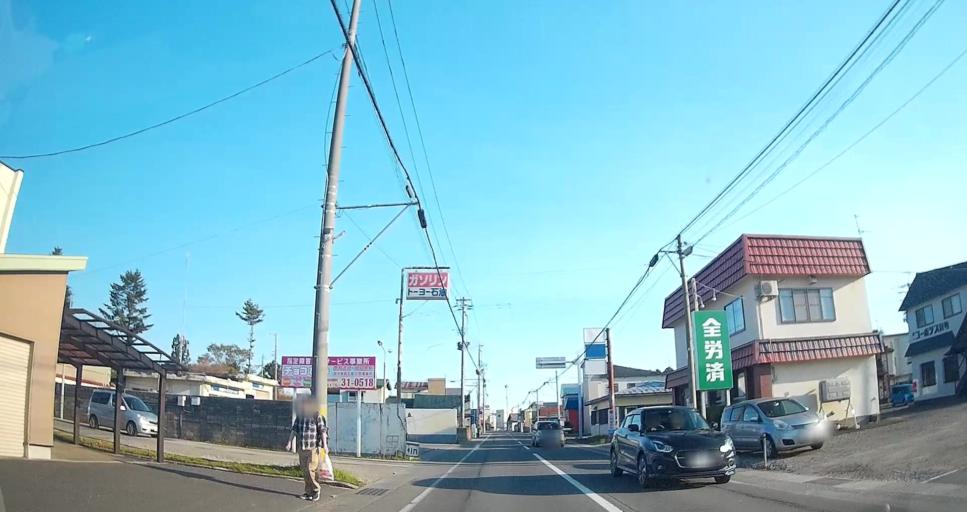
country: JP
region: Aomori
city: Mutsu
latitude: 41.2910
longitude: 141.2108
